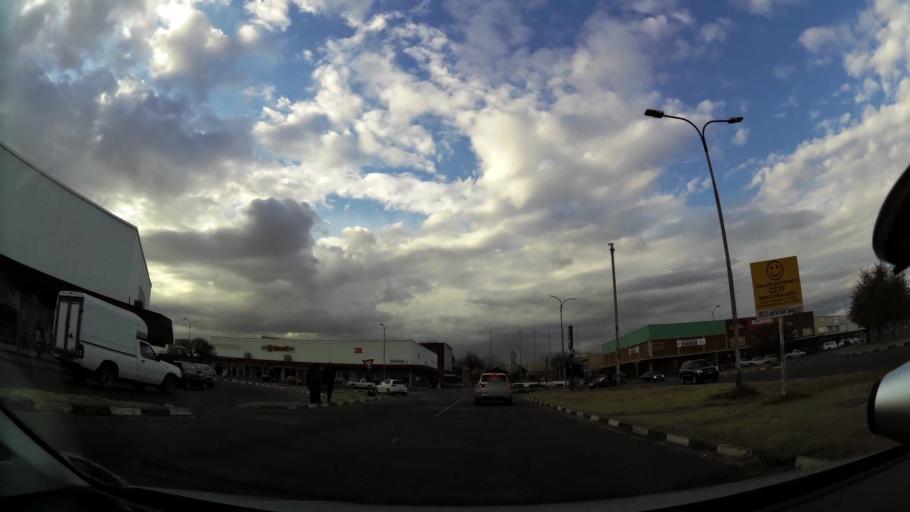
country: ZA
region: Orange Free State
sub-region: Lejweleputswa District Municipality
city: Welkom
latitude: -27.9850
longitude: 26.7360
